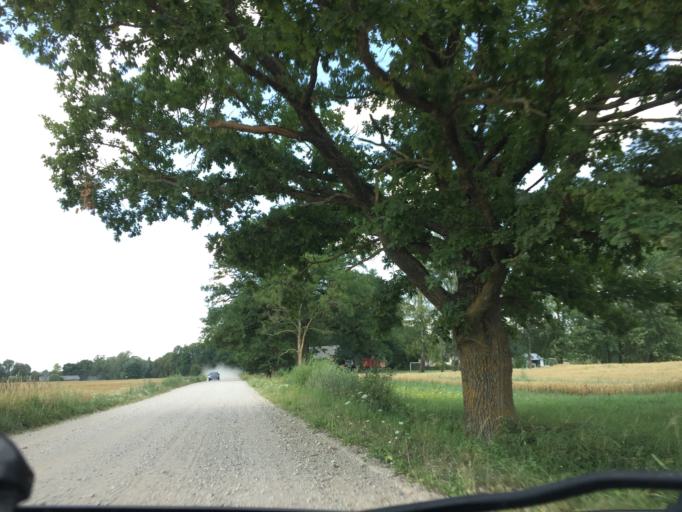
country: LT
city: Zagare
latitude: 56.3936
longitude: 23.2538
